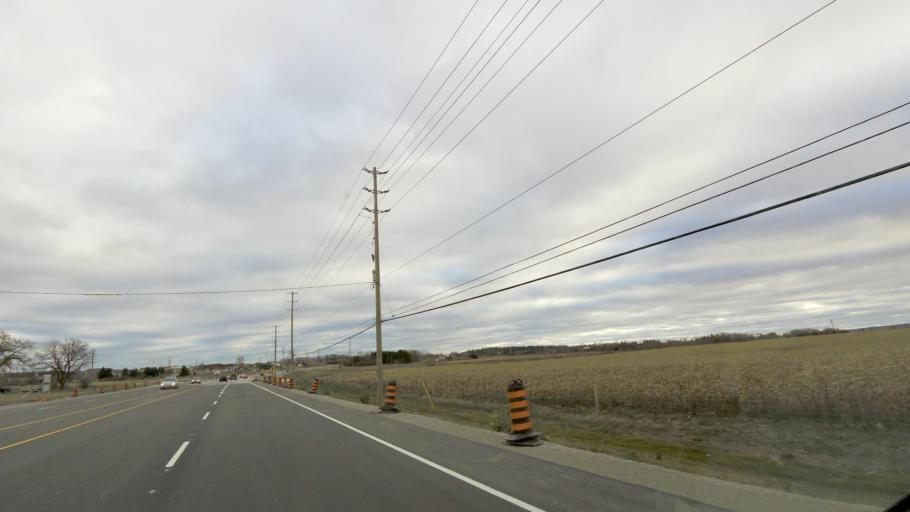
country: CA
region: Ontario
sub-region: Halton
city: Milton
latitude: 43.4700
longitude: -79.8116
